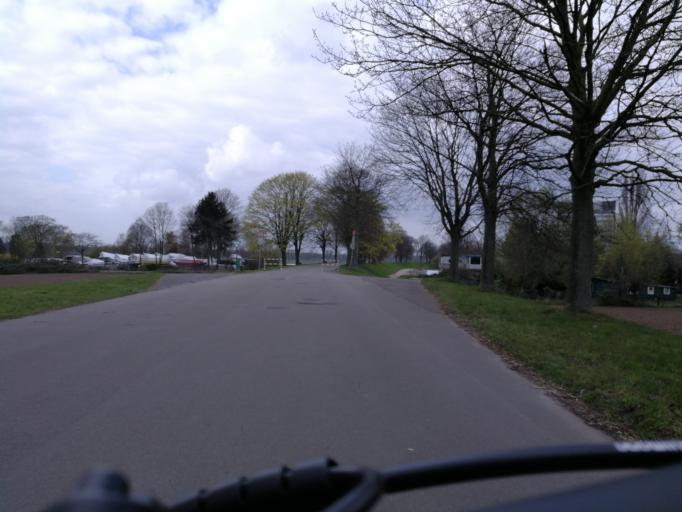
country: DE
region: North Rhine-Westphalia
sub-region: Regierungsbezirk Dusseldorf
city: Dusseldorf
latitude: 51.1856
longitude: 6.7437
